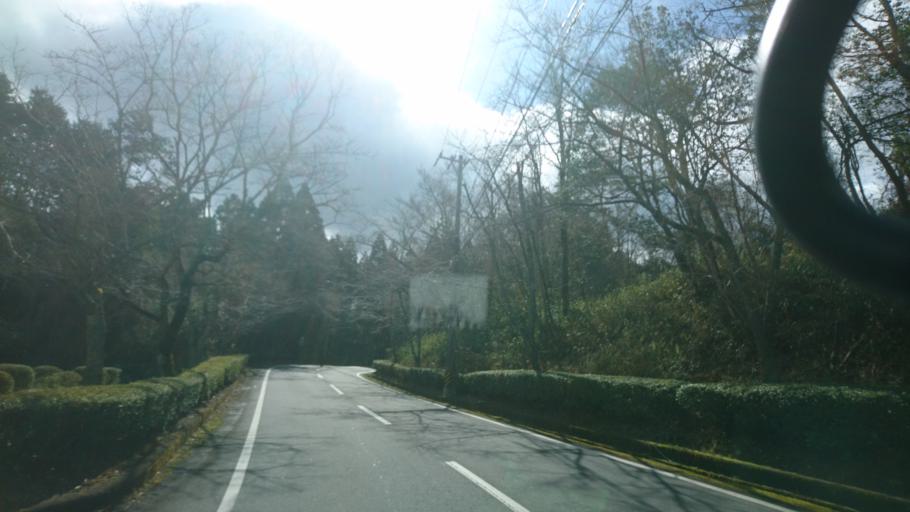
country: JP
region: Mie
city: Ueno-ebisumachi
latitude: 34.7541
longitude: 136.0520
